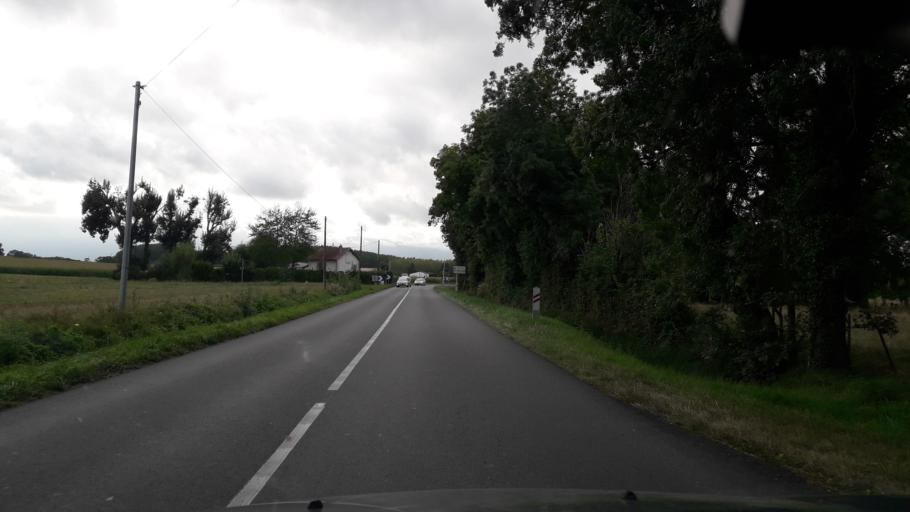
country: FR
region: Poitou-Charentes
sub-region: Departement de la Charente-Maritime
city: Medis
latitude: 45.6750
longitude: -0.9741
